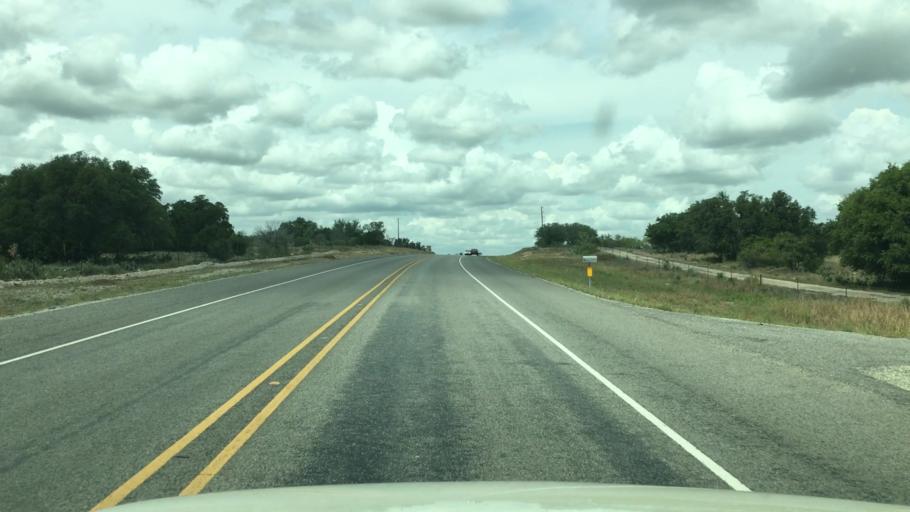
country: US
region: Texas
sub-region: McCulloch County
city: Brady
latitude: 31.0329
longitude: -99.2330
